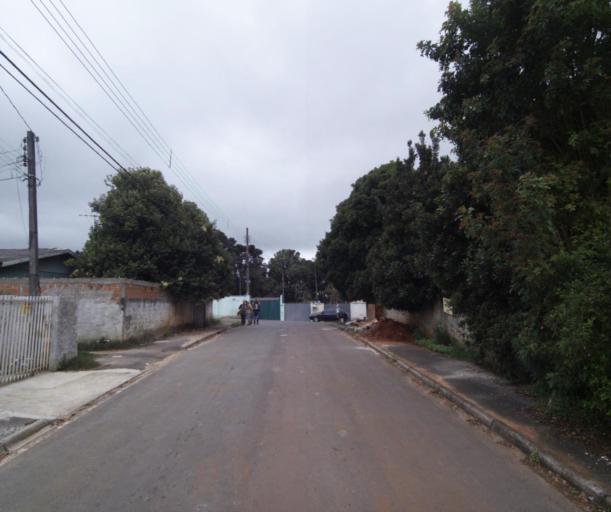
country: BR
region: Parana
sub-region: Quatro Barras
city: Quatro Barras
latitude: -25.3661
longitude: -49.1144
